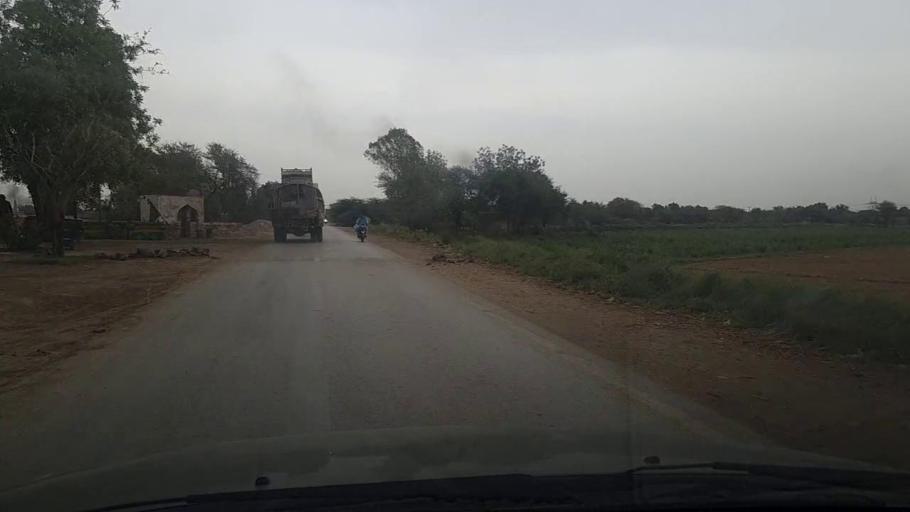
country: PK
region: Sindh
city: Daulatpur
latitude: 26.3389
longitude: 68.1216
